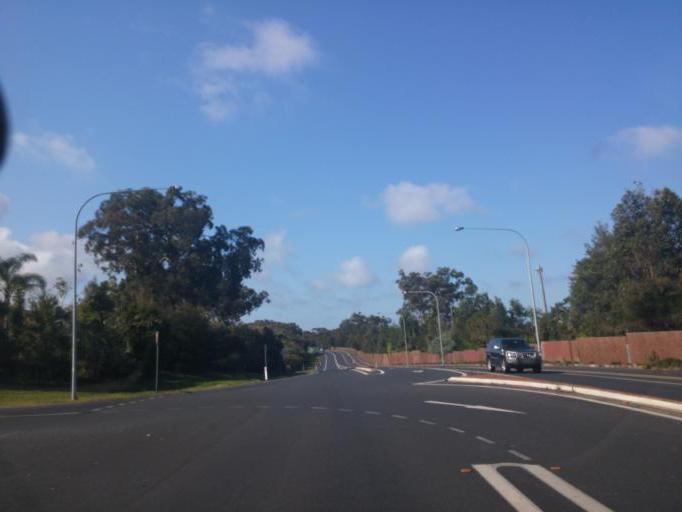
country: AU
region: New South Wales
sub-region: Coffs Harbour
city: Coffs Harbour
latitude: -30.2954
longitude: 153.1303
